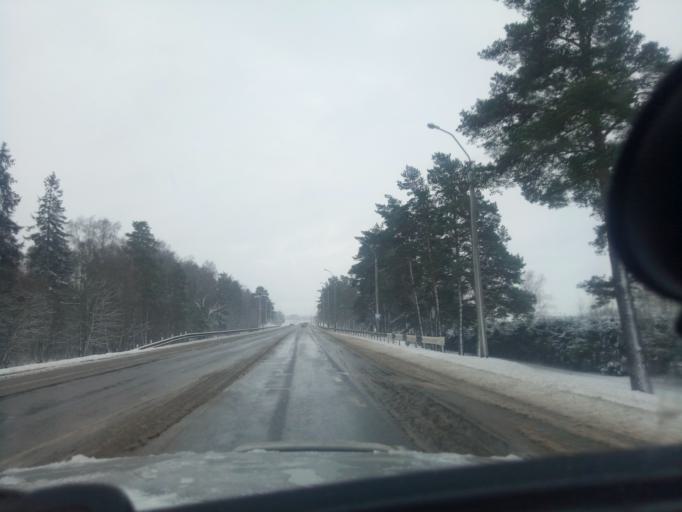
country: BY
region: Minsk
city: Nyasvizh
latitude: 53.2446
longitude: 26.6272
